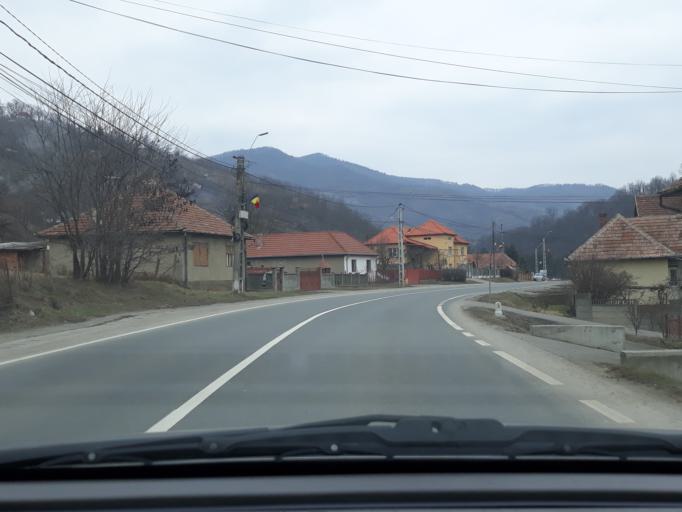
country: RO
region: Salaj
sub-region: Oras Simleu Silvaniei
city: Simleu Silvaniei
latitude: 47.2282
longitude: 22.7792
